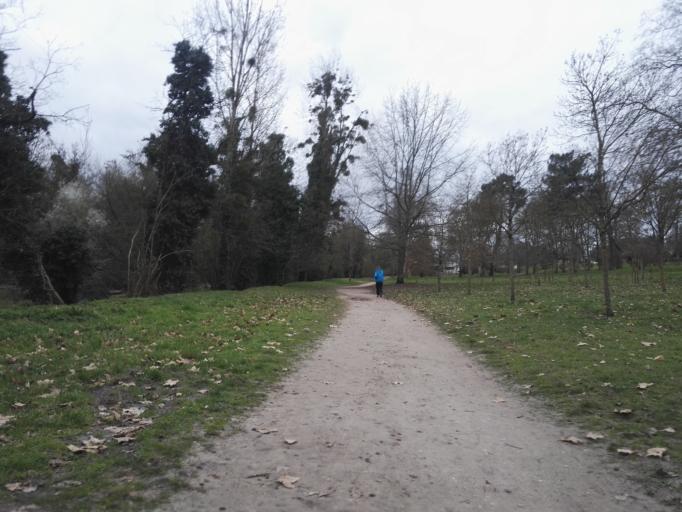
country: FR
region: Aquitaine
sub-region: Departement de la Gironde
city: Begles
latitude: 44.7931
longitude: -0.5577
